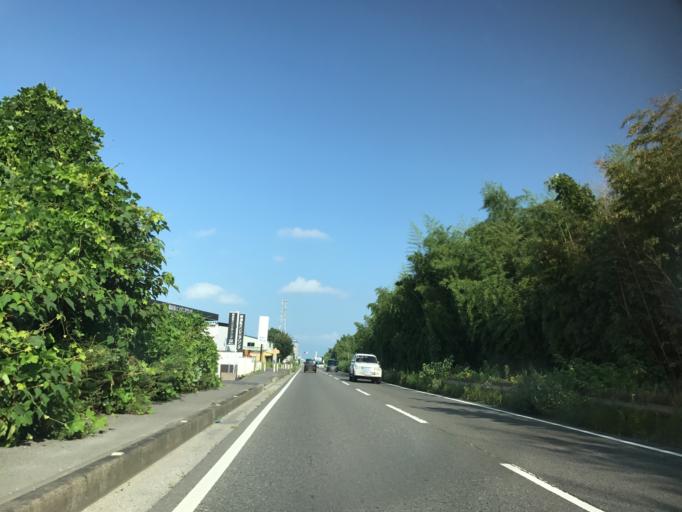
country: JP
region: Shiga Prefecture
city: Moriyama
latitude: 35.0258
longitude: 136.0371
